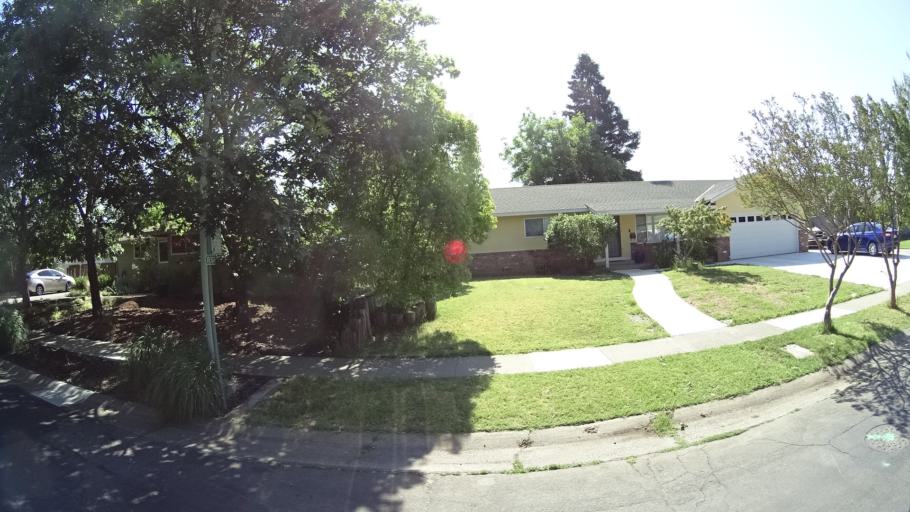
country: US
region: California
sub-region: Sacramento County
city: Florin
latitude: 38.5385
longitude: -121.4212
